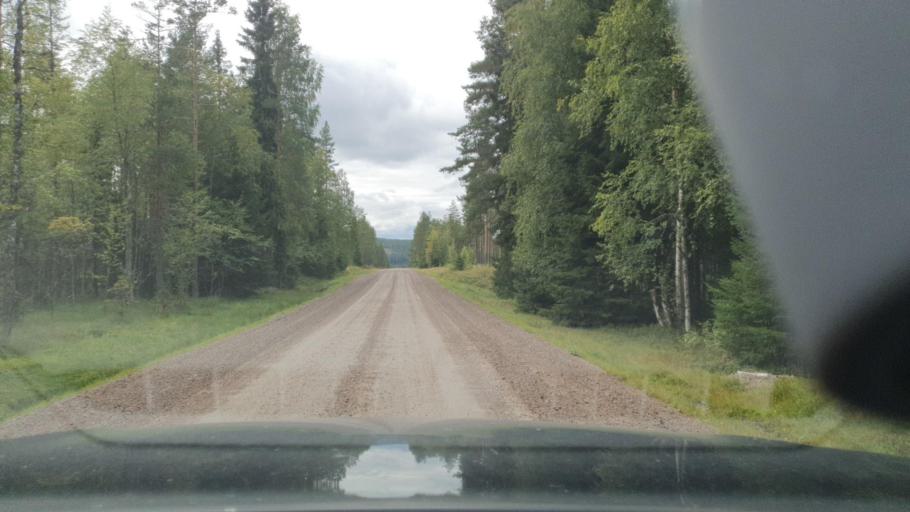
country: SE
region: Vaermland
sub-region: Torsby Kommun
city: Torsby
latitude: 60.5174
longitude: 13.0604
